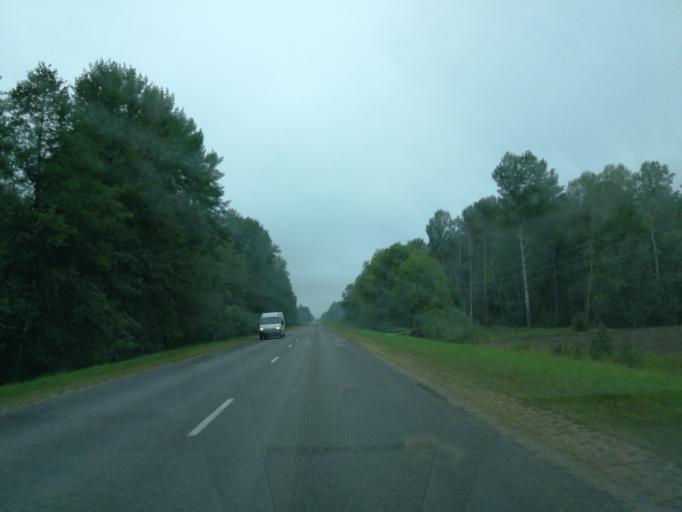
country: LV
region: Varkava
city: Vecvarkava
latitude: 56.3202
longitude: 26.4415
